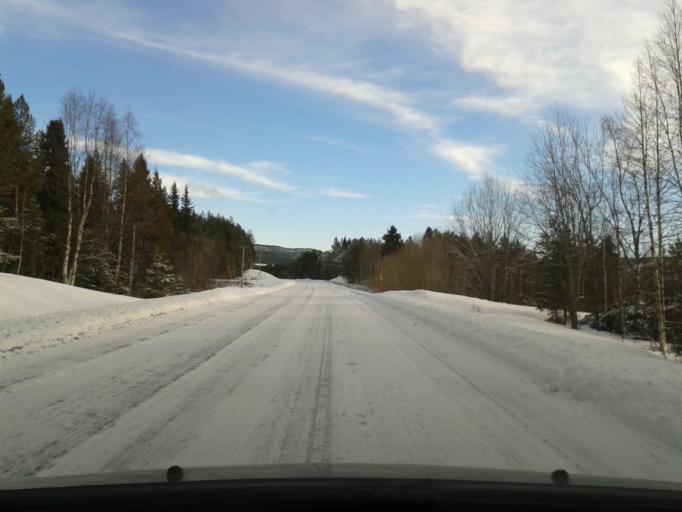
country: SE
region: Vaesterbotten
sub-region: Asele Kommun
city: Asele
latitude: 64.3431
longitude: 17.0105
